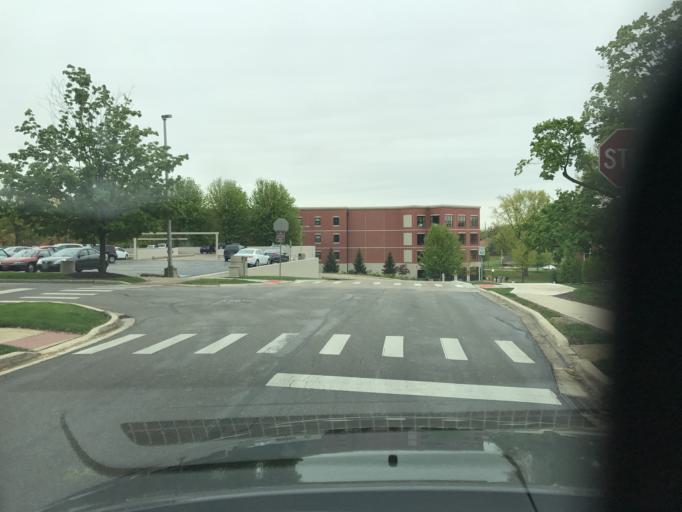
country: US
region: Illinois
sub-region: DuPage County
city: Naperville
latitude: 41.7711
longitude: -88.1437
